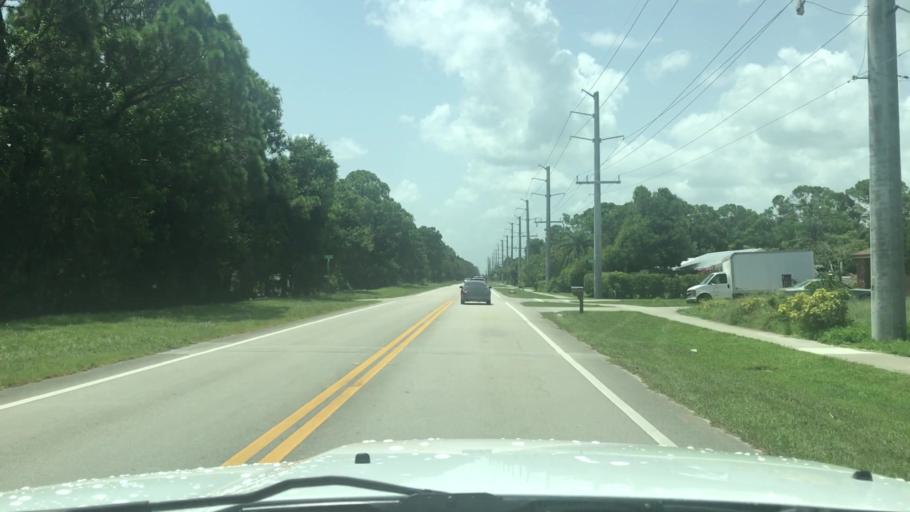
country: US
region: Florida
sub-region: Indian River County
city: Vero Beach South
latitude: 27.6238
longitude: -80.4210
